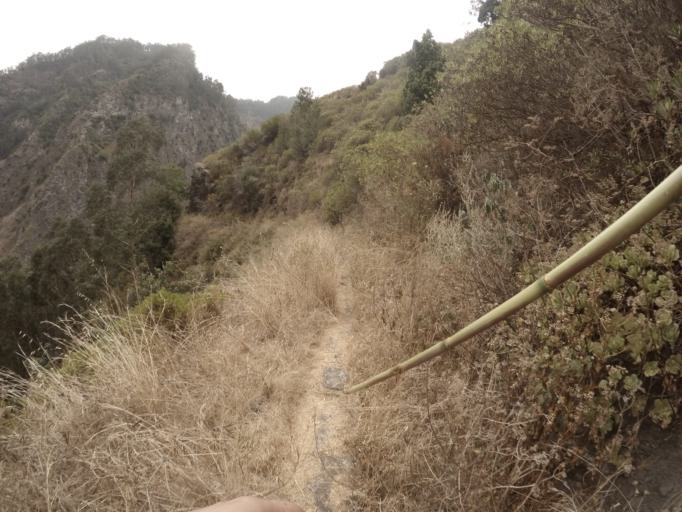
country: PT
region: Madeira
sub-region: Camara de Lobos
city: Curral das Freiras
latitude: 32.7005
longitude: -16.9711
